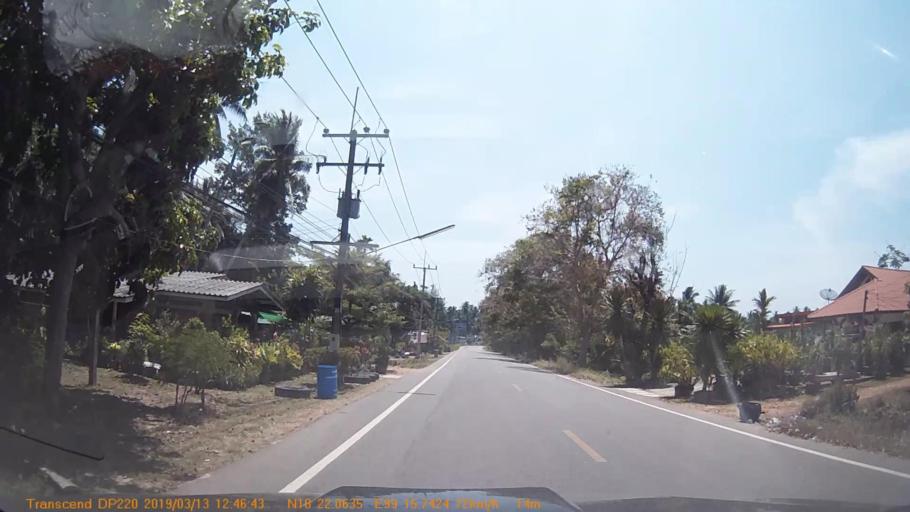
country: TH
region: Chumphon
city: Chumphon
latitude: 10.3672
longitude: 99.2623
